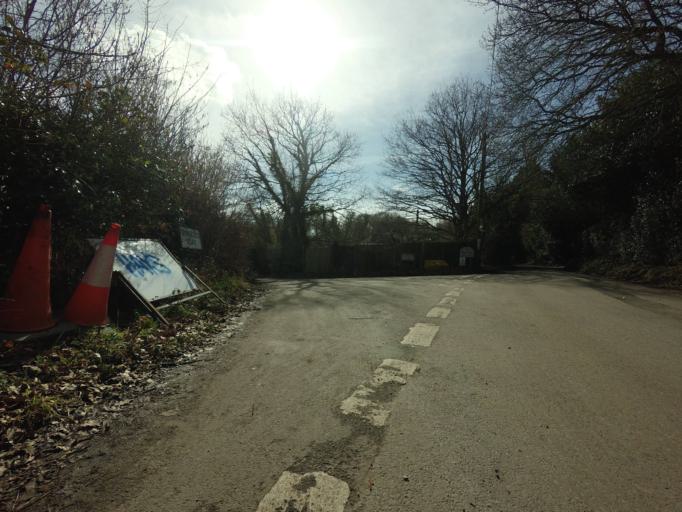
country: GB
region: England
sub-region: Kent
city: Halstead
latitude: 51.3591
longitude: 0.1511
